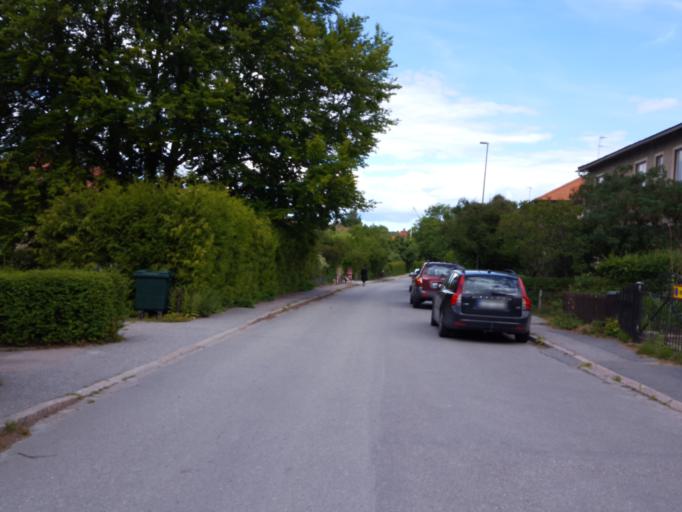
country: SE
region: Uppsala
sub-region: Uppsala Kommun
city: Uppsala
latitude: 59.8437
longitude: 17.6275
